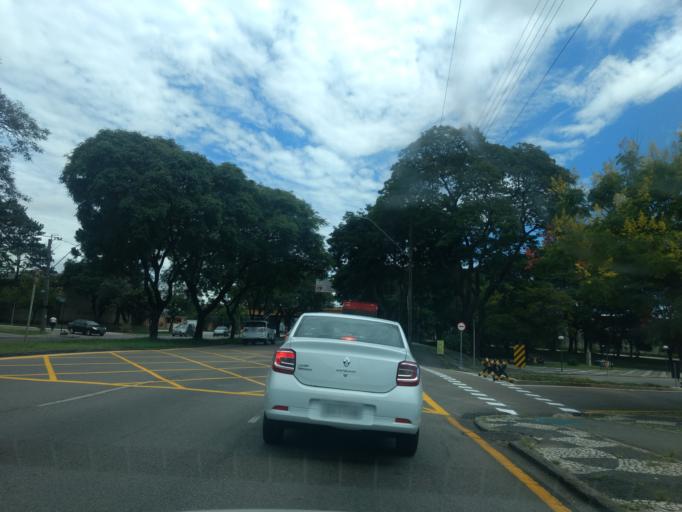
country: BR
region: Parana
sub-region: Pinhais
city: Pinhais
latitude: -25.4286
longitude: -49.2268
